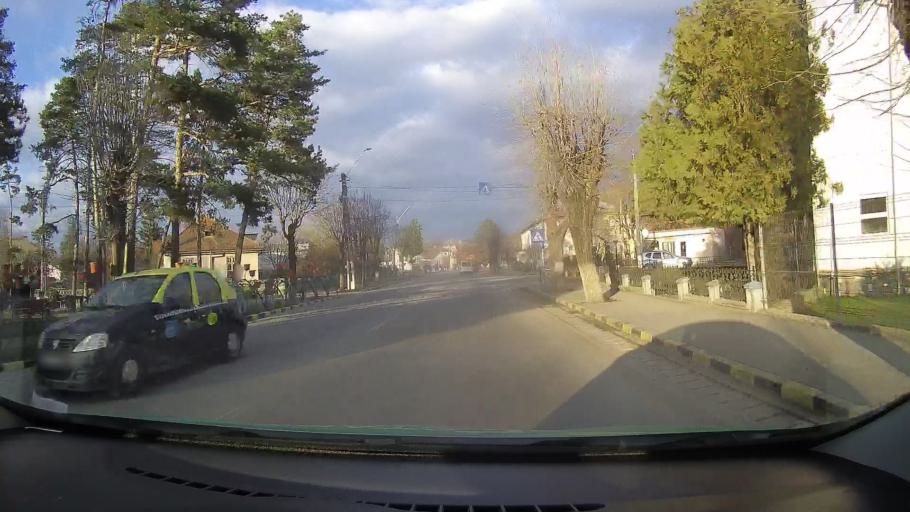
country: RO
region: Dambovita
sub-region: Municipiul Moreni
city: Moreni
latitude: 44.9819
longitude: 25.6395
